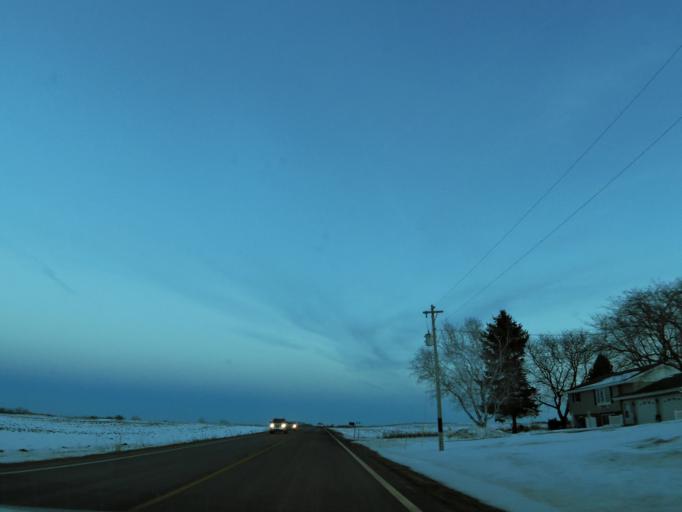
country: US
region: Minnesota
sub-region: Scott County
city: Shakopee
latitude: 44.7328
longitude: -93.5503
